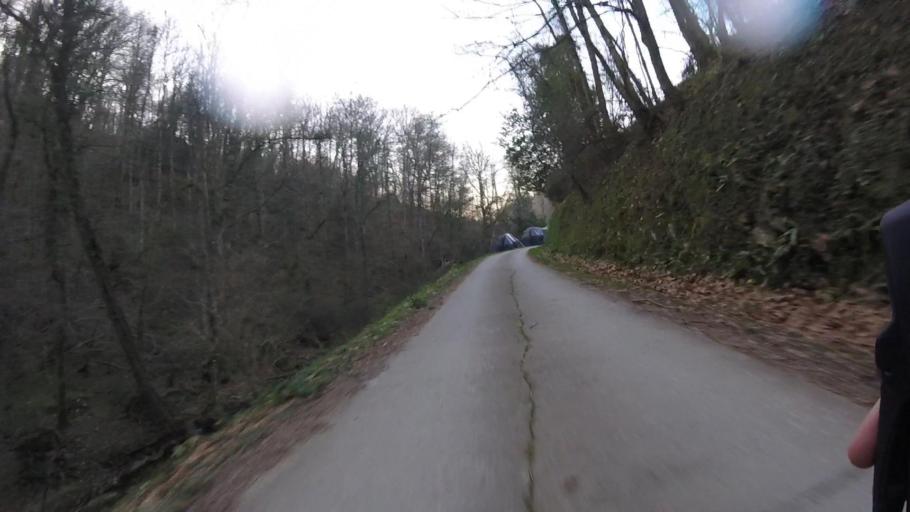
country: ES
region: Basque Country
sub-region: Provincia de Guipuzcoa
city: Errenteria
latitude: 43.2759
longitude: -1.8684
